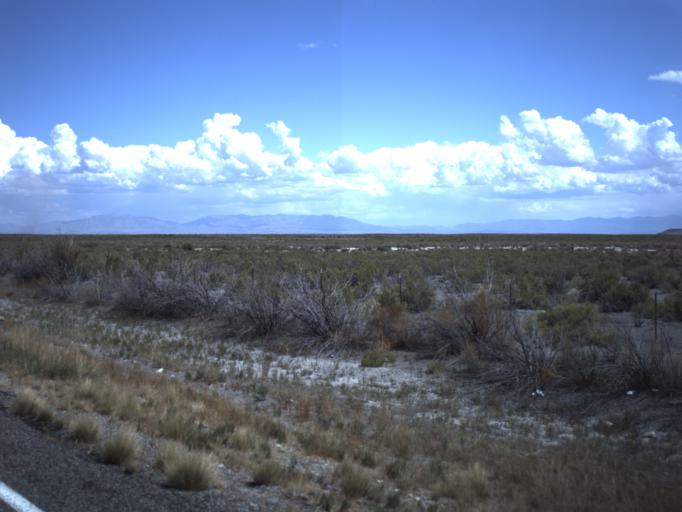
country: US
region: Utah
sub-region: Millard County
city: Delta
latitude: 39.2743
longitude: -112.8563
